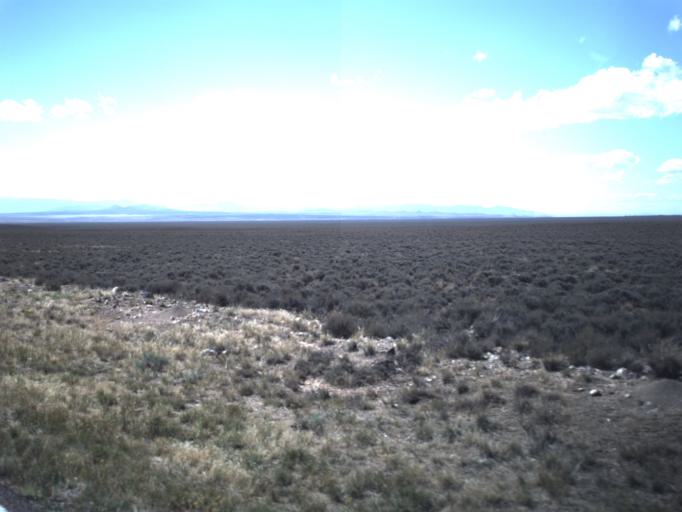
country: US
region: Utah
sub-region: Iron County
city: Enoch
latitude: 37.9698
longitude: -113.0063
